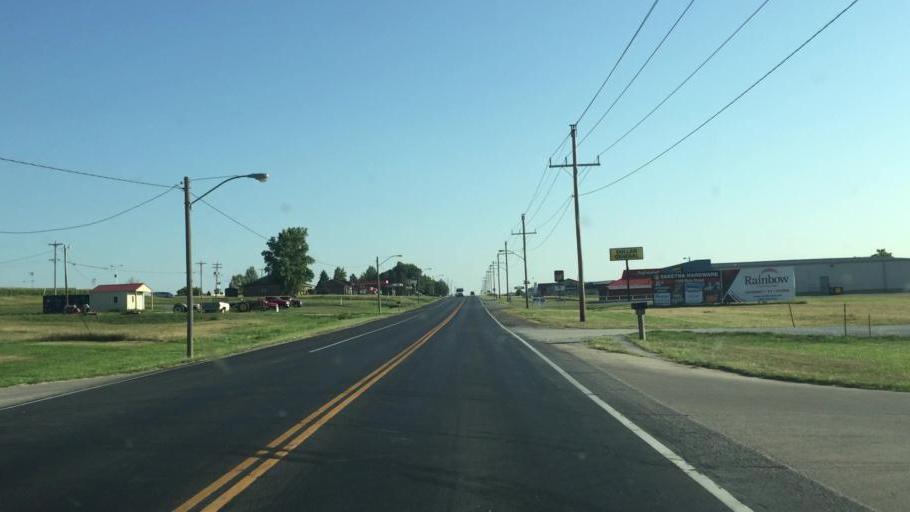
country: US
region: Kansas
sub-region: Nemaha County
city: Sabetha
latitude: 39.8904
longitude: -95.7883
